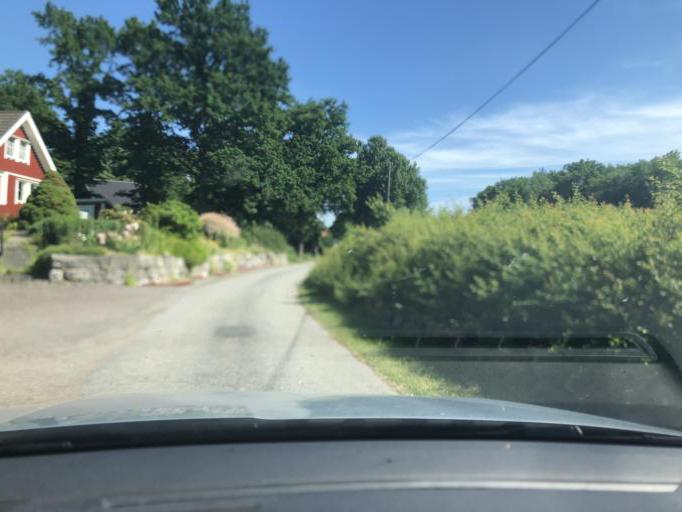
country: SE
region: Blekinge
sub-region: Karlshamns Kommun
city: Morrum
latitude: 56.1890
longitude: 14.6978
